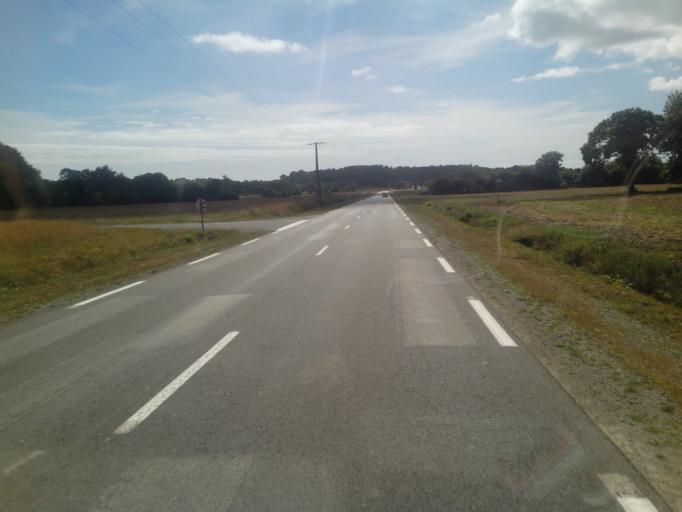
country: FR
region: Brittany
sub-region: Departement du Morbihan
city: Peaule
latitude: 47.5712
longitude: -2.3851
